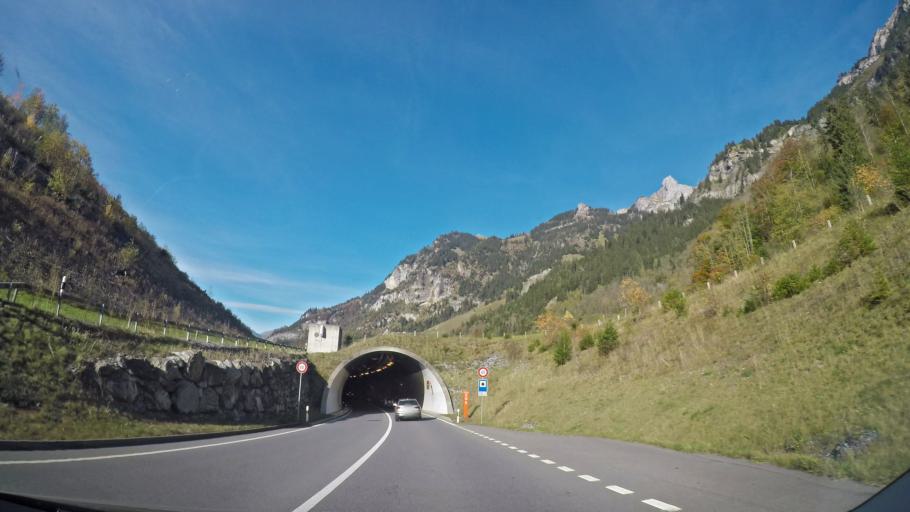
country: CH
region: Bern
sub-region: Frutigen-Niedersimmental District
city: Kandersteg
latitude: 46.5165
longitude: 7.6787
